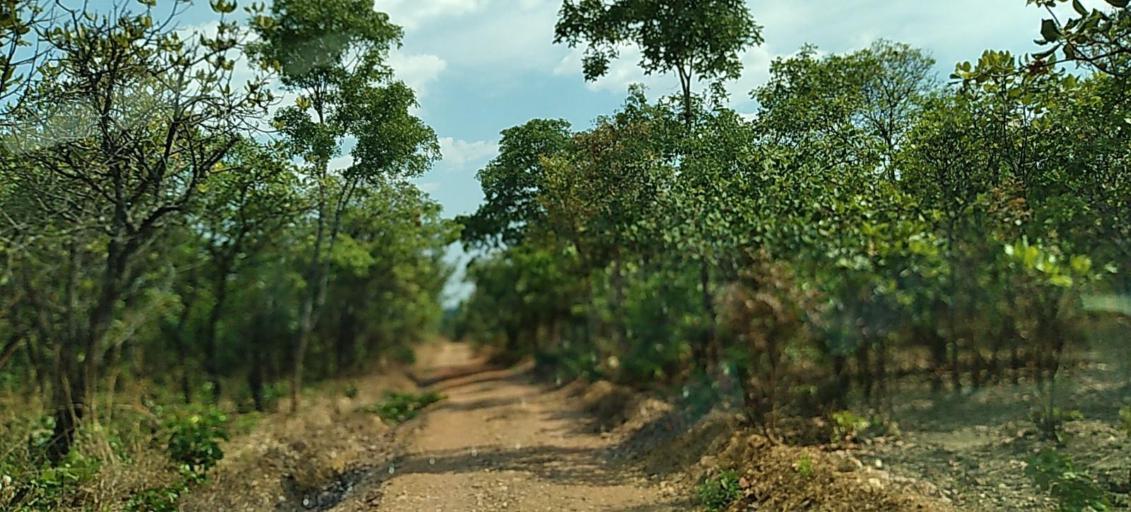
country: ZM
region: Copperbelt
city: Chililabombwe
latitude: -12.3239
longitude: 27.7879
